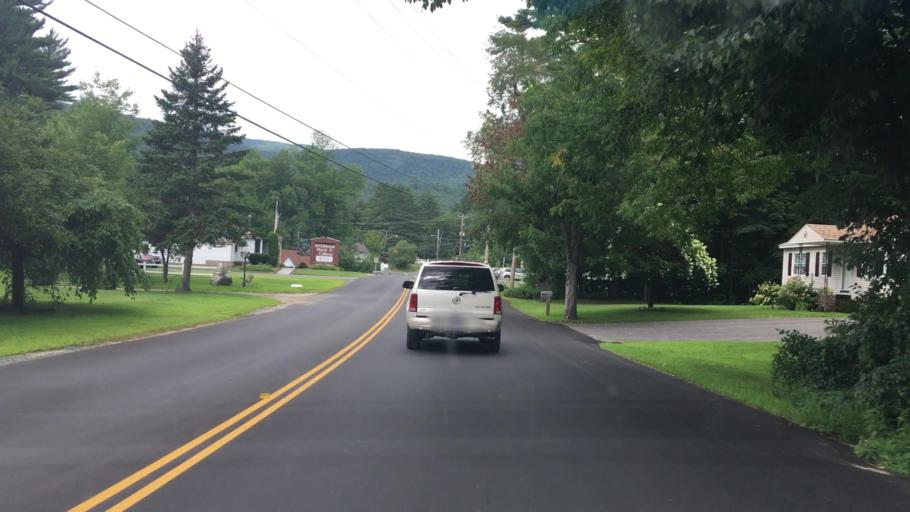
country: US
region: New Hampshire
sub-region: Grafton County
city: Woodstock
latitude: 44.0456
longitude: -71.6841
